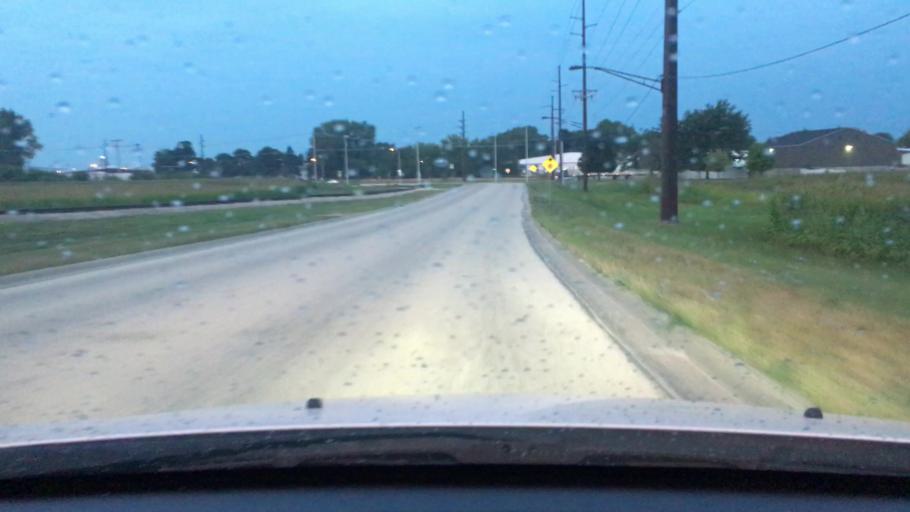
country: US
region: Illinois
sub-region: Ogle County
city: Rochelle
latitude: 41.9215
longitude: -89.0545
